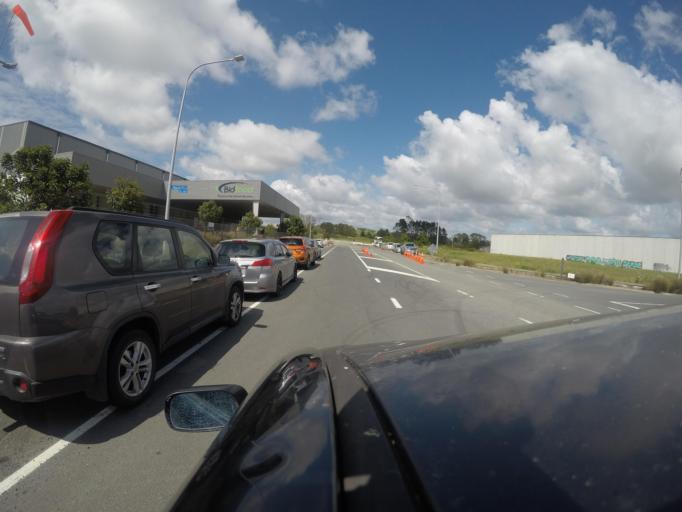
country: NZ
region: Auckland
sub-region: Auckland
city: Rosebank
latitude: -36.8059
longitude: 174.6325
